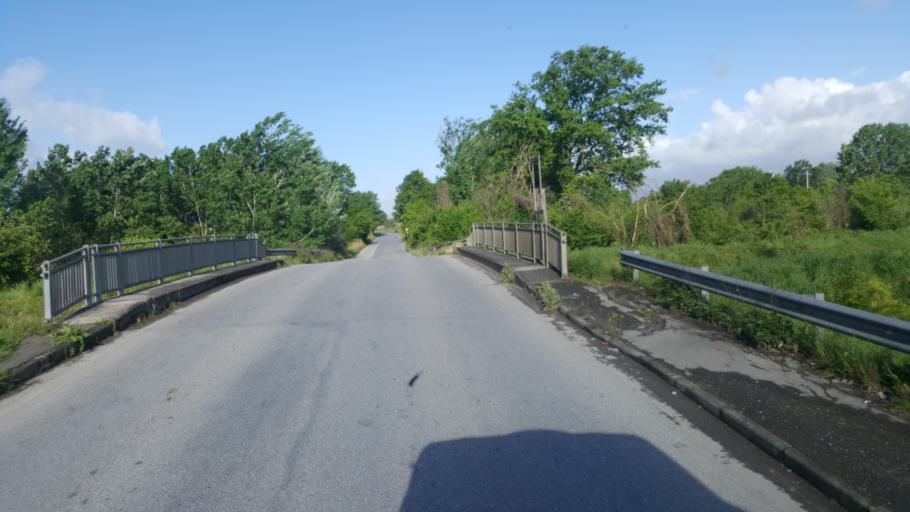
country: IT
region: Tuscany
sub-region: Provincia di Lucca
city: Porcari
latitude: 43.8500
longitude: 10.5961
